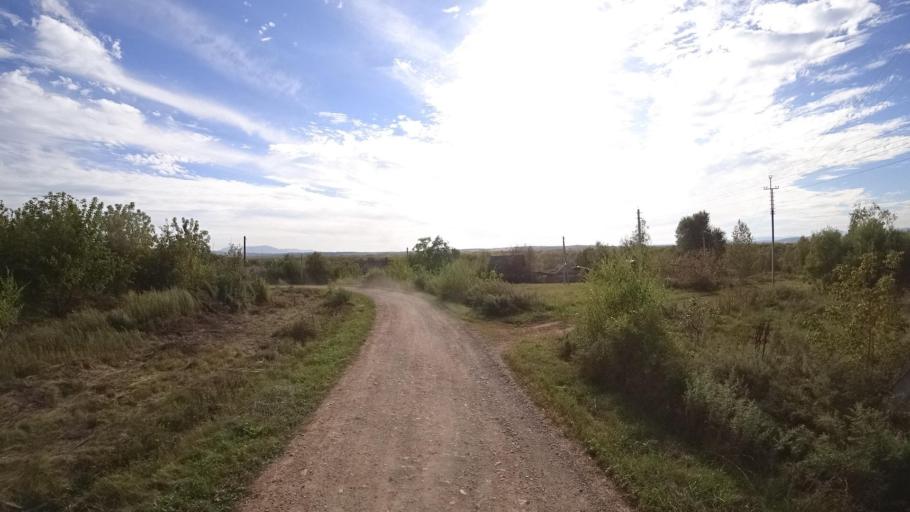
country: RU
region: Primorskiy
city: Dostoyevka
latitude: 44.2961
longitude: 133.4487
